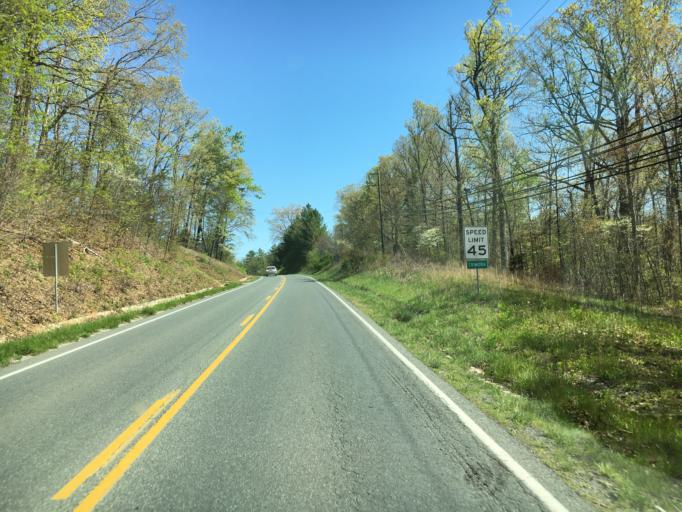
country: US
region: Virginia
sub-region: Augusta County
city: Crimora
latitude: 38.1451
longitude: -78.8417
